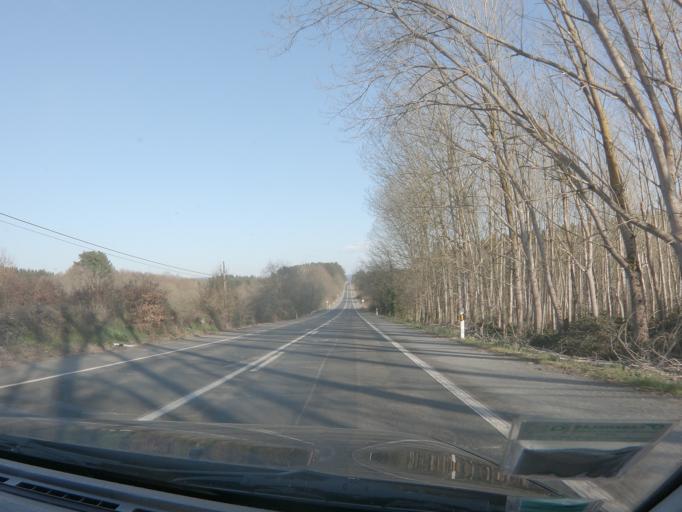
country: ES
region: Galicia
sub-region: Provincia de Lugo
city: Corgo
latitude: 42.9400
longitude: -7.4214
